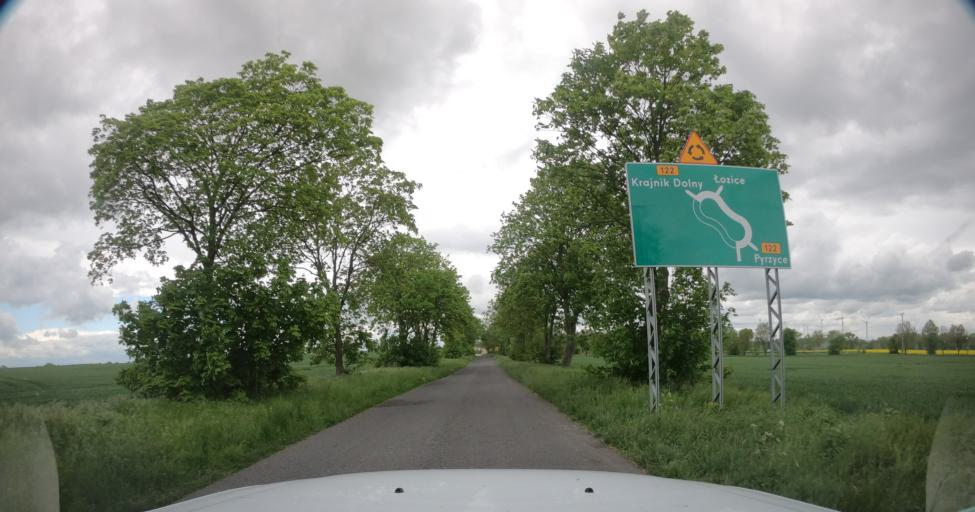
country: PL
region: West Pomeranian Voivodeship
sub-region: Powiat pyrzycki
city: Kozielice
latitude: 53.1223
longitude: 14.7994
